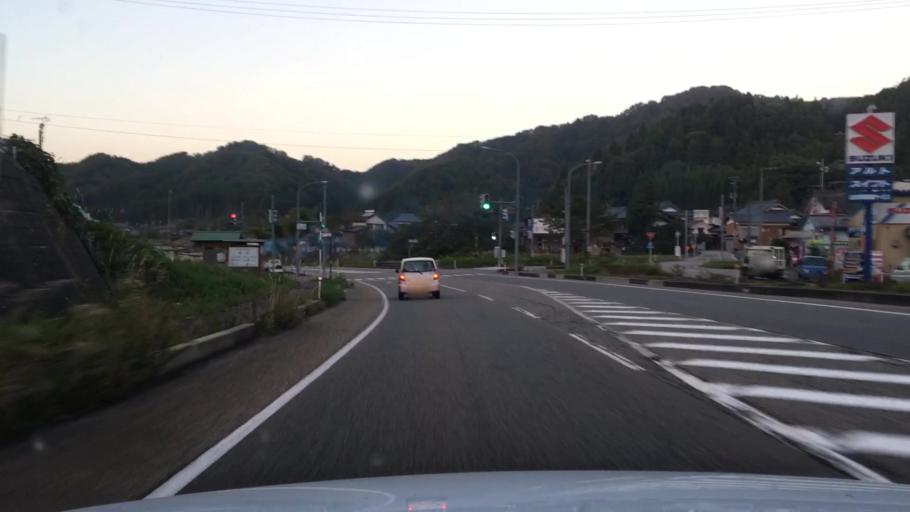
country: JP
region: Niigata
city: Murakami
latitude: 38.4364
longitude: 139.5907
